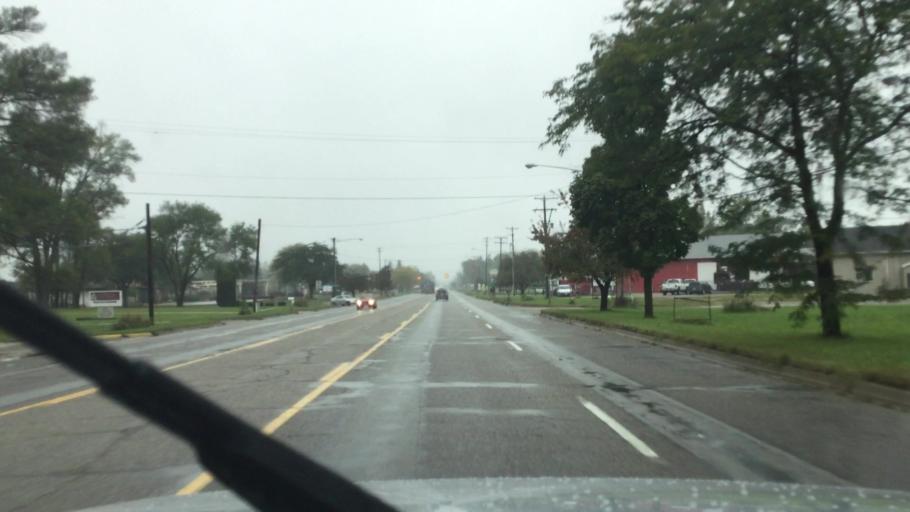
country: US
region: Michigan
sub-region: Saginaw County
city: Bridgeport
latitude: 43.3770
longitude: -83.8947
